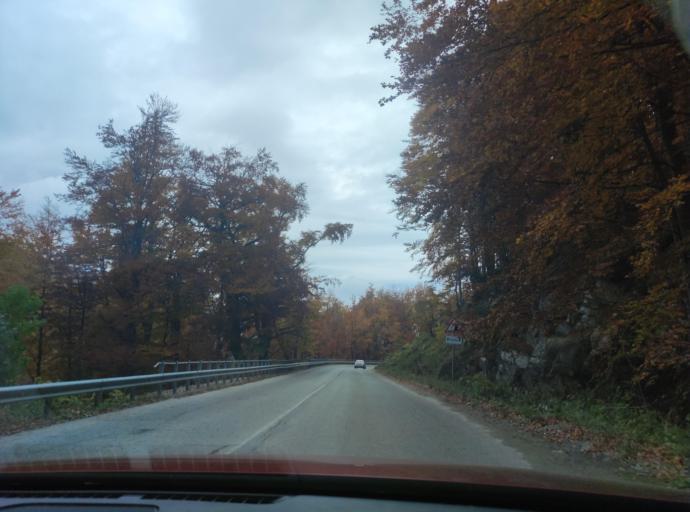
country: BG
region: Montana
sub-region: Obshtina Berkovitsa
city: Berkovitsa
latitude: 43.1266
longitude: 23.1397
